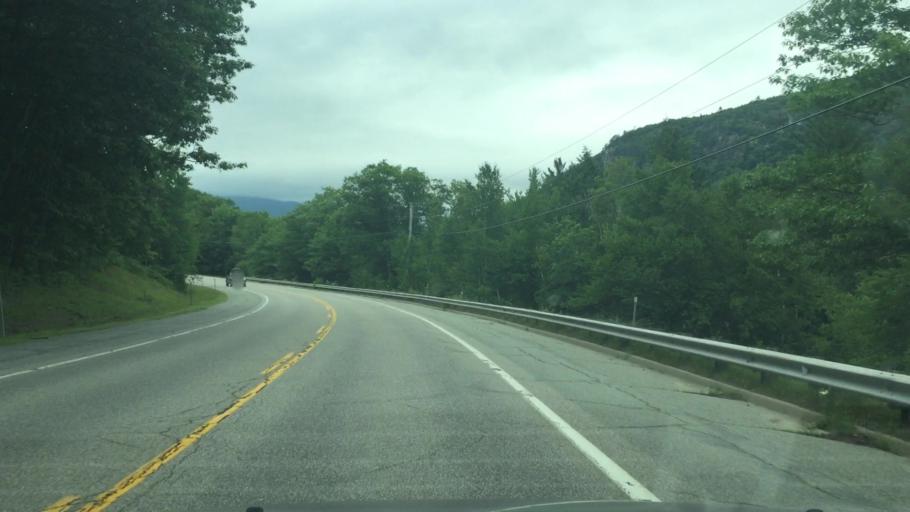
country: US
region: New Hampshire
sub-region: Carroll County
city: North Conway
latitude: 44.1202
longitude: -71.3543
